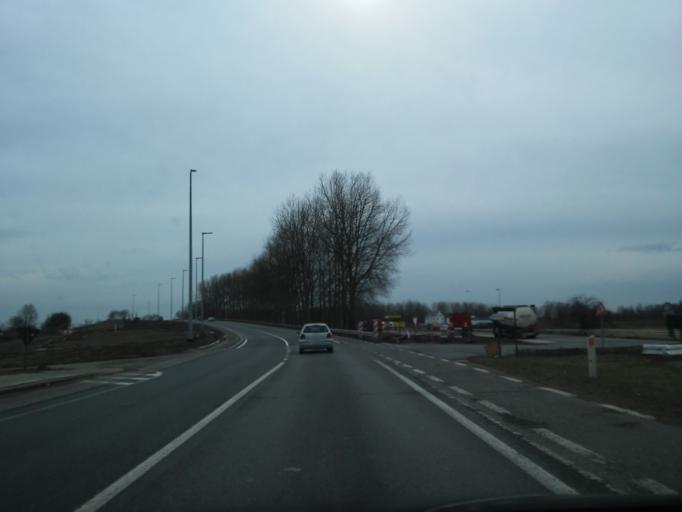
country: BE
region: Flanders
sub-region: Provincie Oost-Vlaanderen
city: Hamme
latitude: 51.1101
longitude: 4.1423
